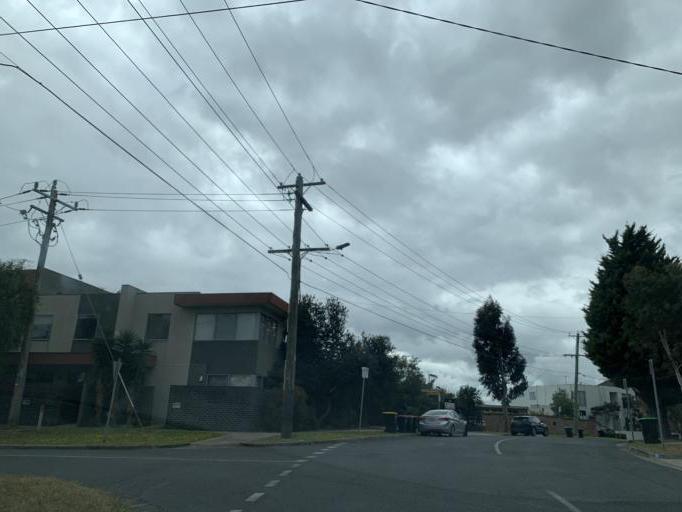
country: AU
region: Victoria
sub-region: Kingston
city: Mentone
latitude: -37.9809
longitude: 145.0762
